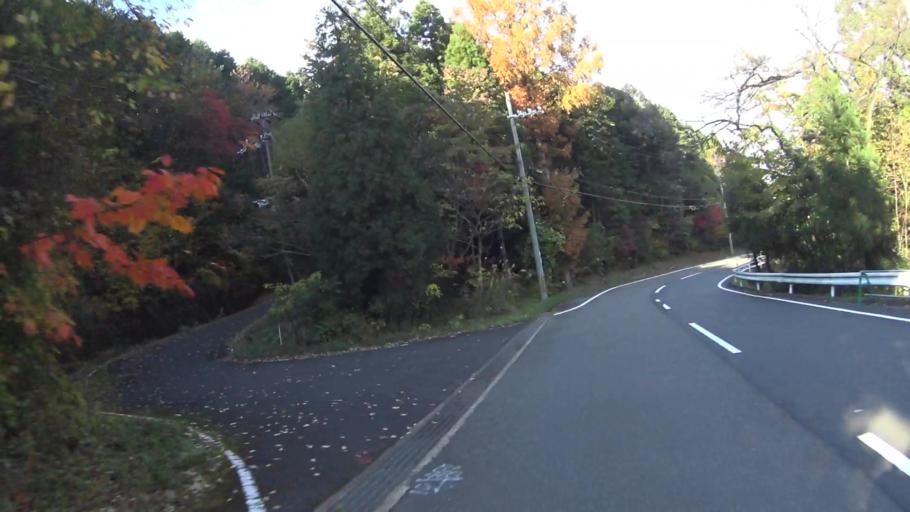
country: JP
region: Kyoto
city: Maizuru
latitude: 35.5464
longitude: 135.3957
